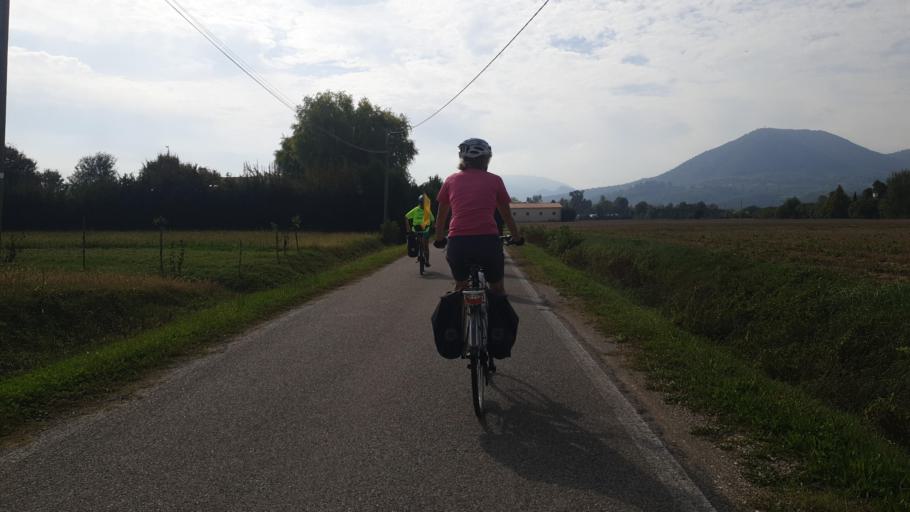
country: IT
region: Veneto
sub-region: Provincia di Padova
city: Montemerlo
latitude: 45.3962
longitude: 11.6912
